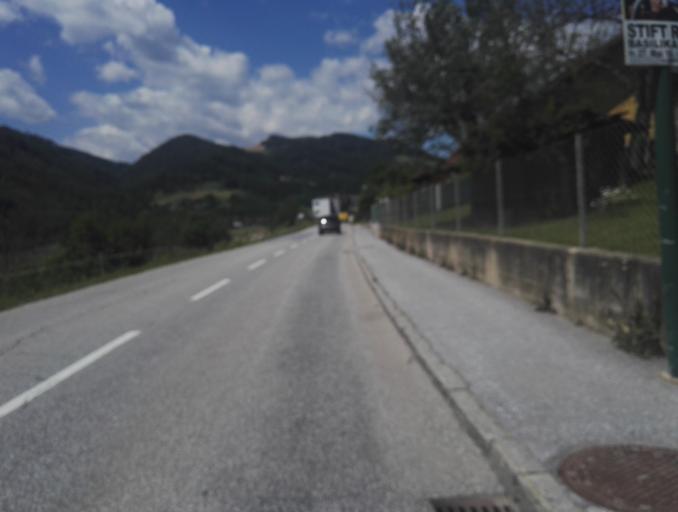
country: AT
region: Styria
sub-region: Politischer Bezirk Graz-Umgebung
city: Deutschfeistritz
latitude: 47.2076
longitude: 15.3245
